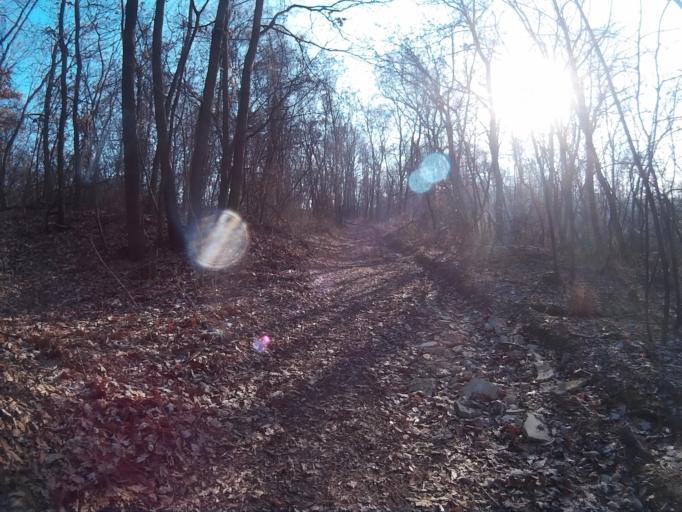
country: HU
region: Nograd
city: Bercel
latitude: 47.9134
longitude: 19.3909
